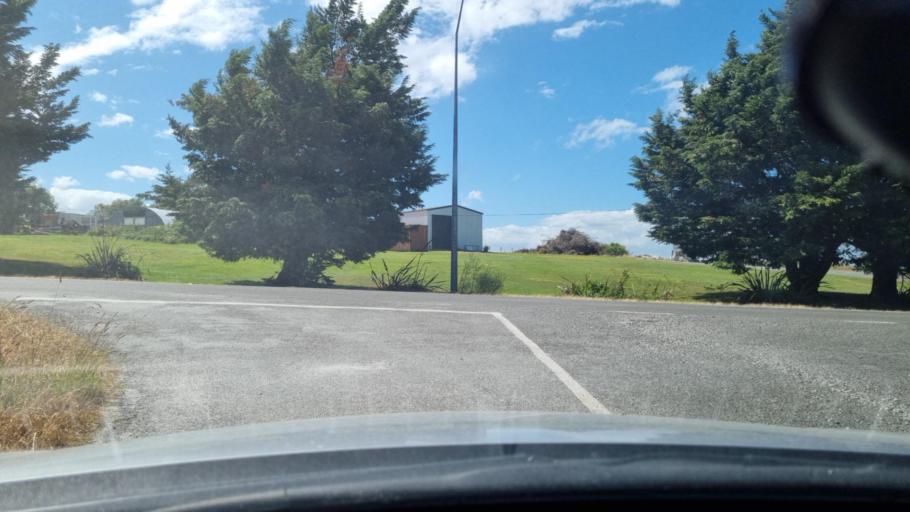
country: NZ
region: Southland
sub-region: Invercargill City
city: Invercargill
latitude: -46.4325
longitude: 168.3896
